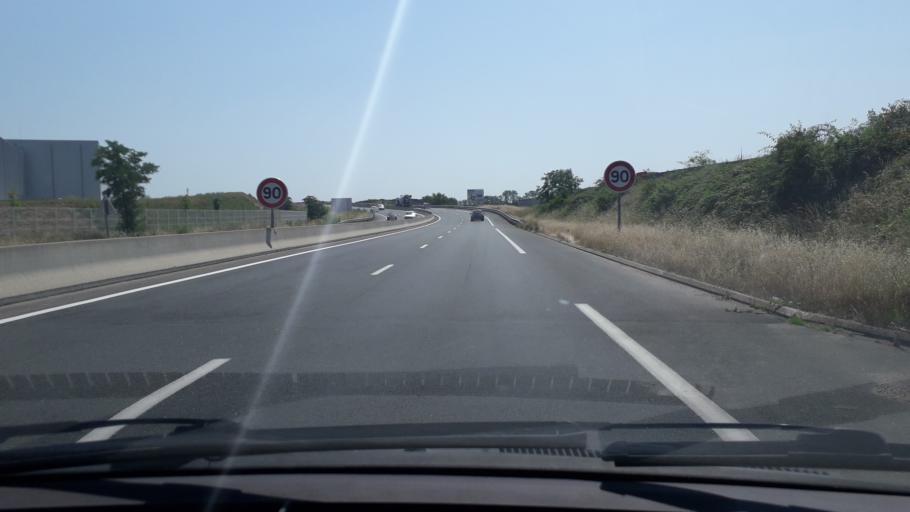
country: FR
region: Rhone-Alpes
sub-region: Departement du Rhone
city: Pusignan
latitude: 45.7665
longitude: 5.0767
